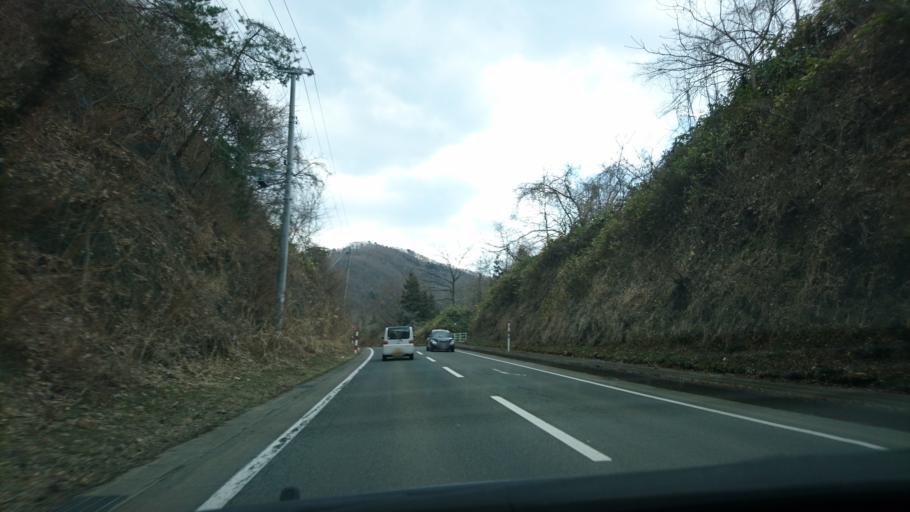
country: JP
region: Iwate
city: Shizukuishi
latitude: 39.6910
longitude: 141.0327
